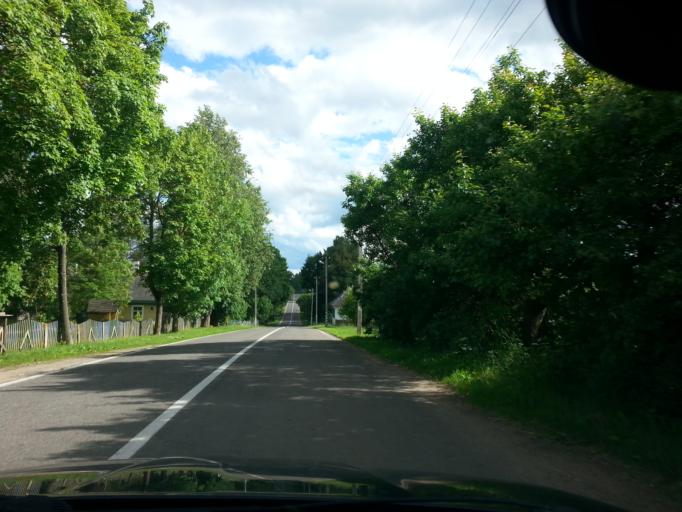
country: BY
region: Minsk
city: Svir
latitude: 54.9000
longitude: 26.3863
